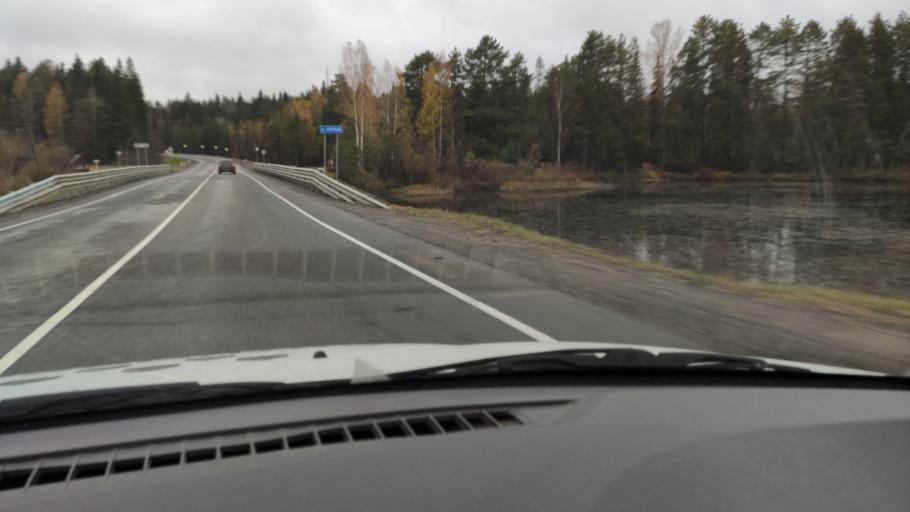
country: RU
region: Kirov
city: Belaya Kholunitsa
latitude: 58.9049
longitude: 50.9460
